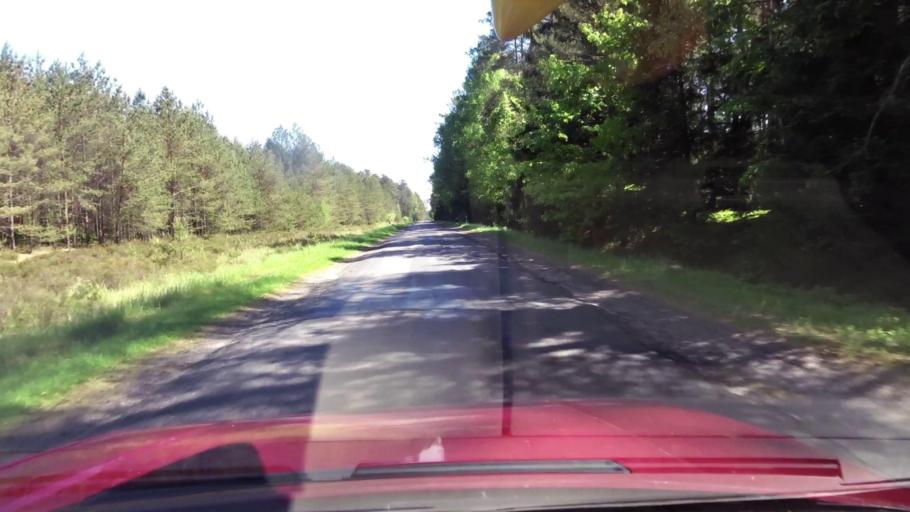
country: PL
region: West Pomeranian Voivodeship
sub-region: Powiat koszalinski
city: Sianow
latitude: 54.0783
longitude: 16.4193
